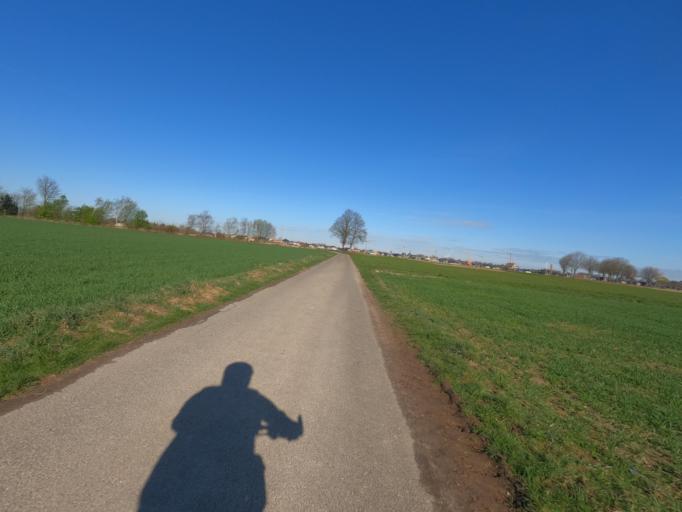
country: DE
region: North Rhine-Westphalia
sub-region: Regierungsbezirk Koln
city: Gangelt
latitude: 50.9974
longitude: 6.0598
